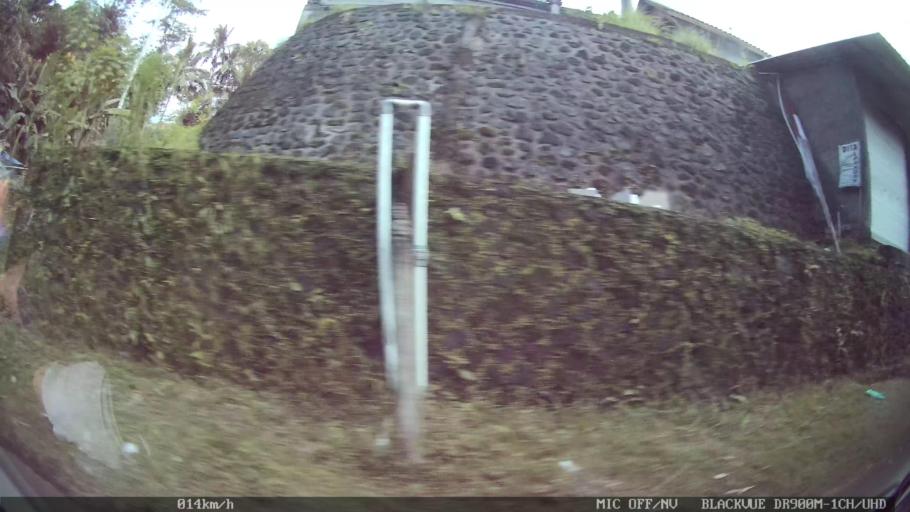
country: ID
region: Bali
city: Banjar Pesalakan
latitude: -8.5064
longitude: 115.3075
